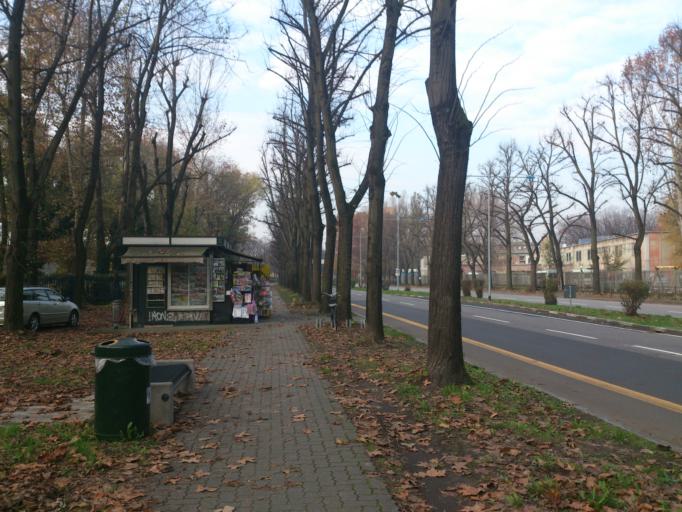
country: IT
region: Lombardy
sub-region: Citta metropolitana di Milano
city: San Donato Milanese
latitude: 45.4187
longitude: 9.2767
